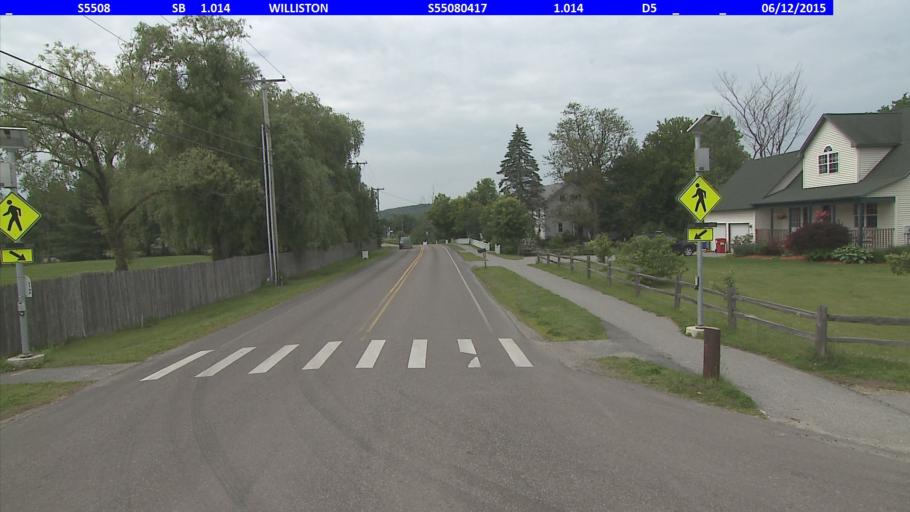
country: US
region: Vermont
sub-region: Chittenden County
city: Williston
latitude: 44.4507
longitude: -73.0599
